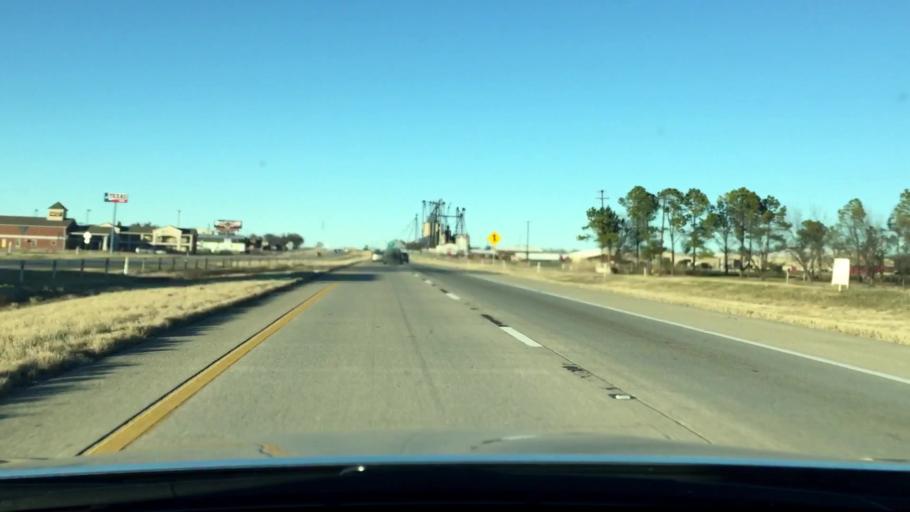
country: US
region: Texas
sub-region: Denton County
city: Sanger
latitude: 33.4754
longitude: -97.1627
